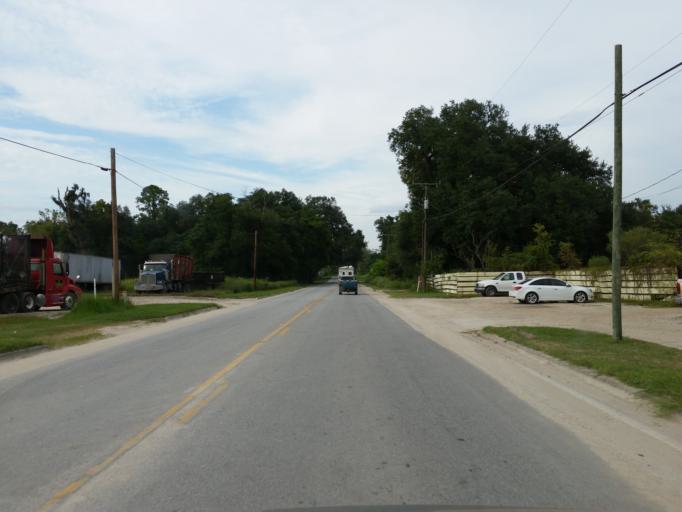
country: US
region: Florida
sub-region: Suwannee County
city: Live Oak
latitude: 30.3067
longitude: -82.9842
